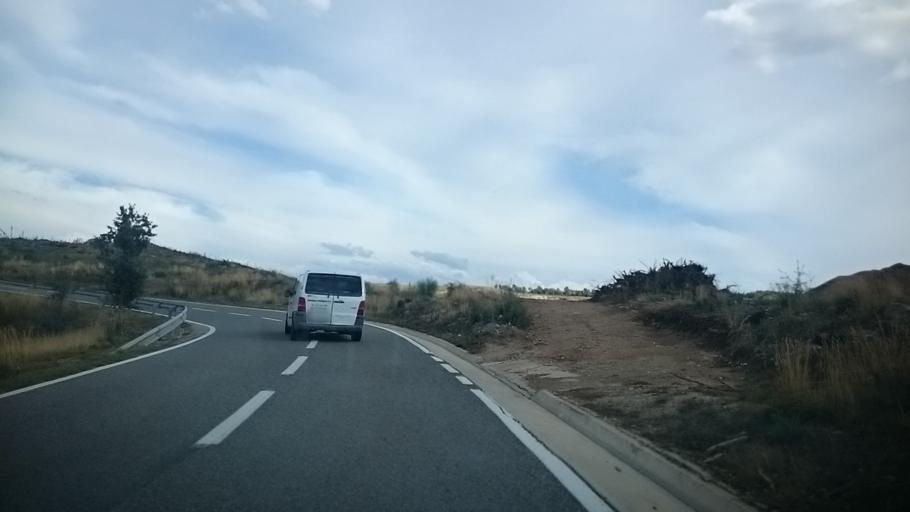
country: ES
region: Catalonia
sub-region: Provincia de Barcelona
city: Odena
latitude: 41.6267
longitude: 1.6747
